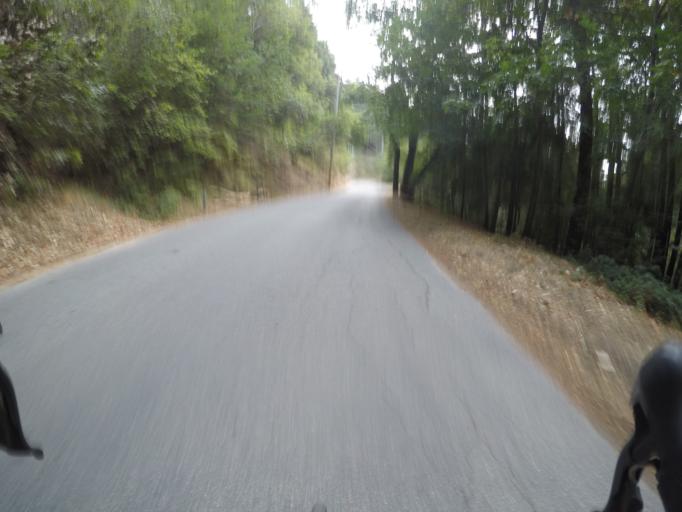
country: US
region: California
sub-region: Santa Cruz County
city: Scotts Valley
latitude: 37.0622
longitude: -122.0179
